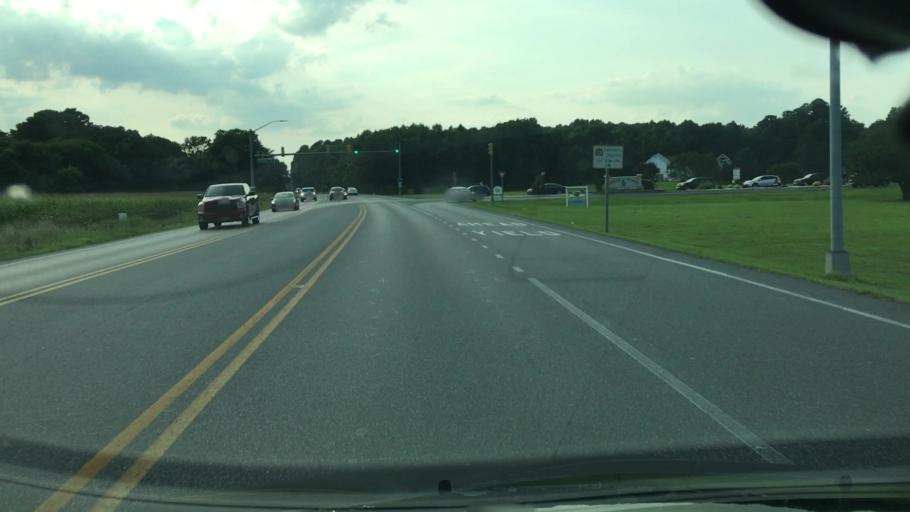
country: US
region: Maryland
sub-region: Worcester County
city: Ocean Pines
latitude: 38.3834
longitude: -75.1763
